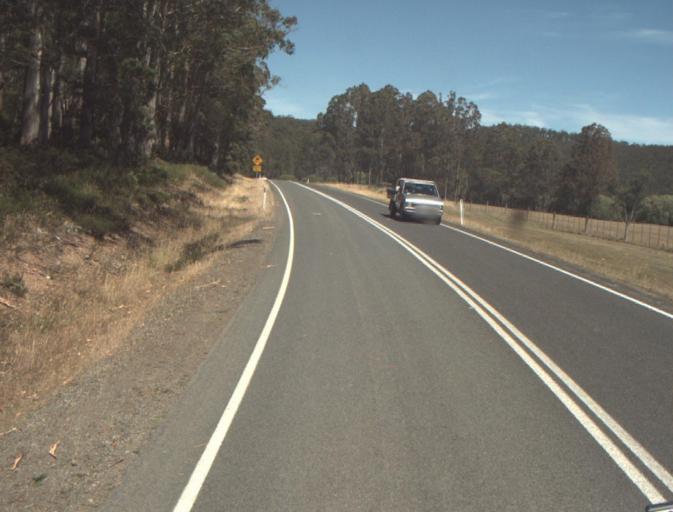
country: AU
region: Tasmania
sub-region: Dorset
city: Scottsdale
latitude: -41.3019
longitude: 147.3818
